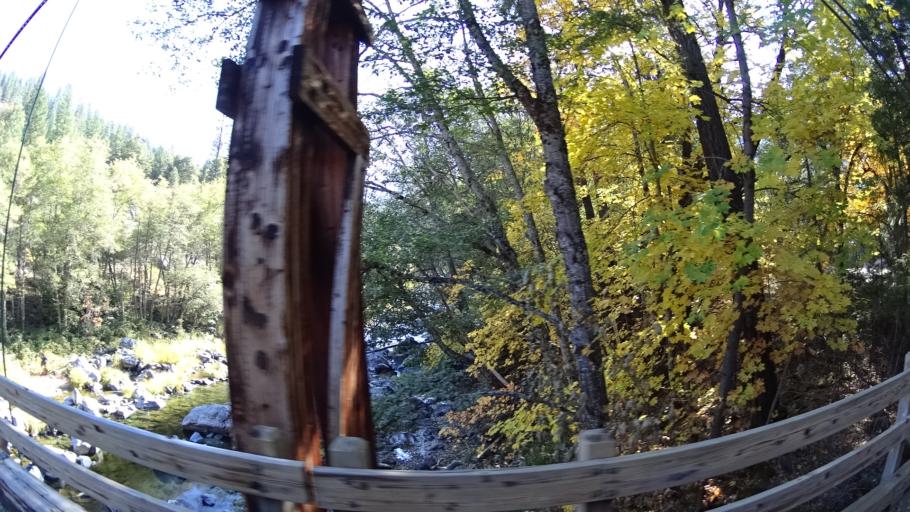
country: US
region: California
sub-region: Siskiyou County
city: Happy Camp
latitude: 41.6339
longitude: -123.1058
